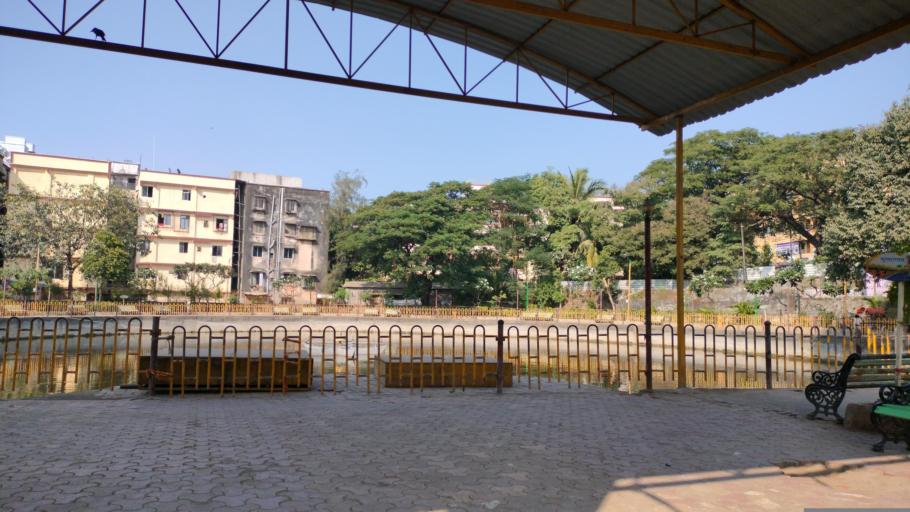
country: IN
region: Maharashtra
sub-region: Thane
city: Virar
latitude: 19.4365
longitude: 72.8224
